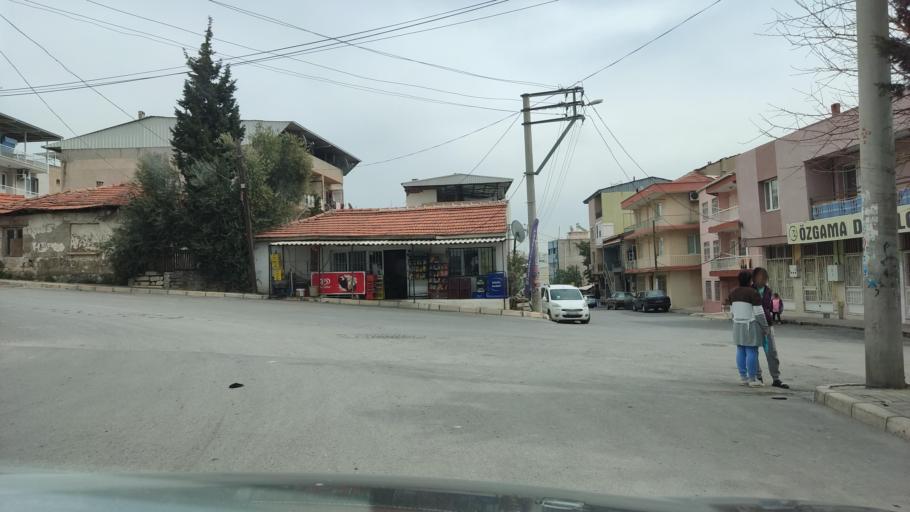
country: TR
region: Izmir
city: Karsiyaka
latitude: 38.4965
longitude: 27.0715
